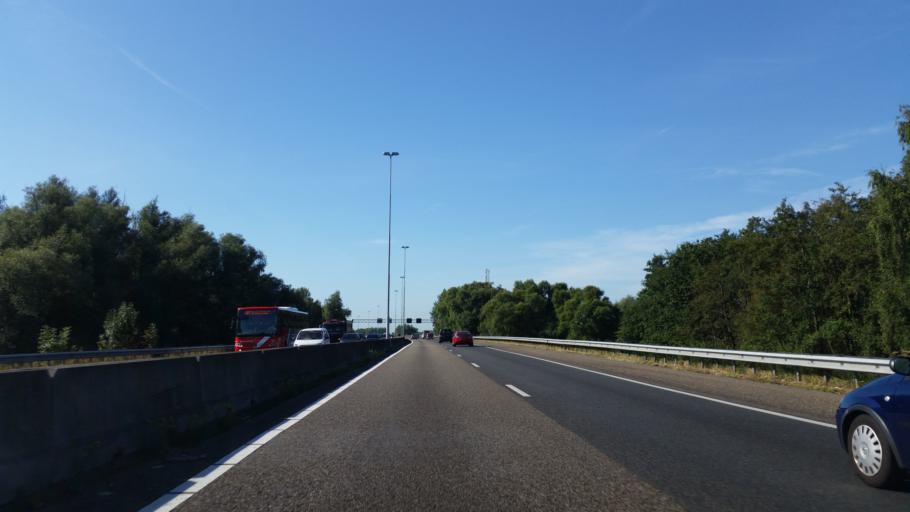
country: NL
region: Utrecht
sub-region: Gemeente Lopik
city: Lopik
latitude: 51.9345
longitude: 4.9988
